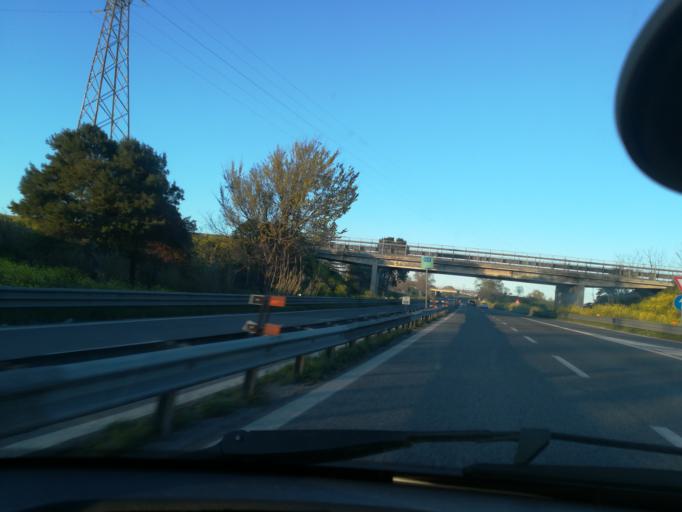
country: IT
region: The Marches
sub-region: Provincia di Macerata
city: Santa Maria Apparente
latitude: 43.2881
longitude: 13.7086
